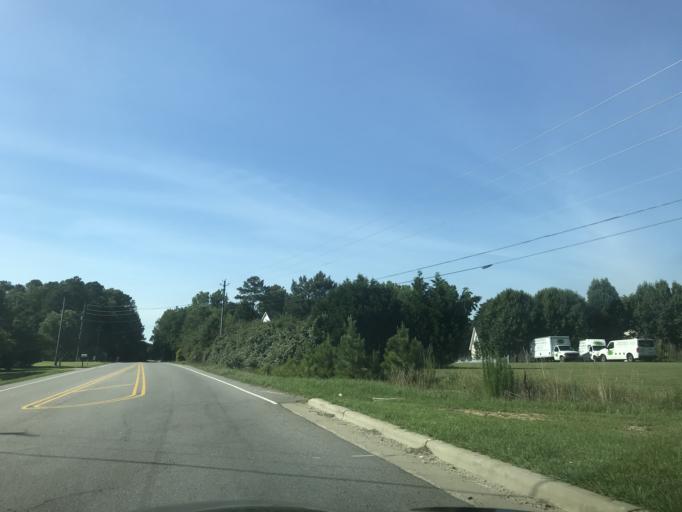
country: US
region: North Carolina
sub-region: Johnston County
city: Clayton
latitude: 35.6186
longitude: -78.5356
